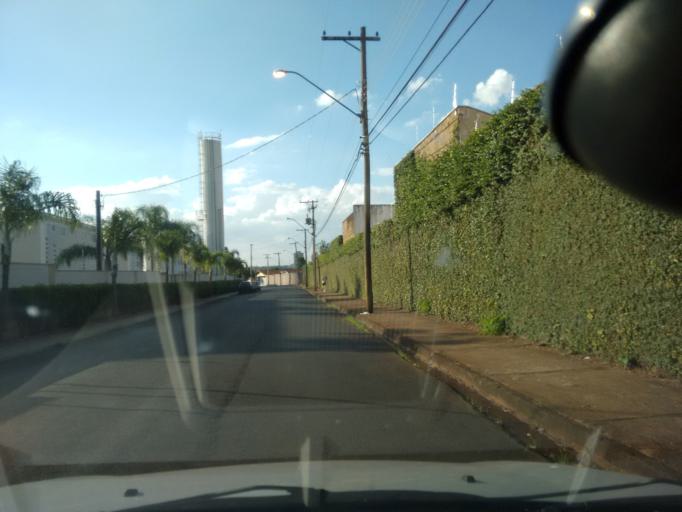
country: BR
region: Sao Paulo
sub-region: Araraquara
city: Araraquara
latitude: -21.7996
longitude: -48.1942
